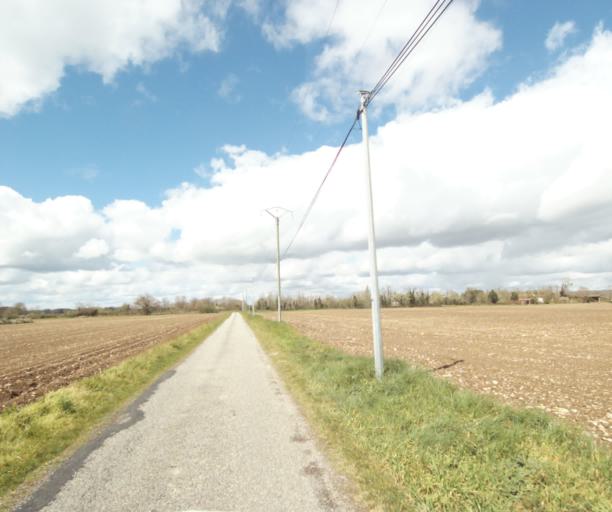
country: FR
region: Midi-Pyrenees
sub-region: Departement de l'Ariege
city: Saverdun
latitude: 43.2566
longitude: 1.5985
